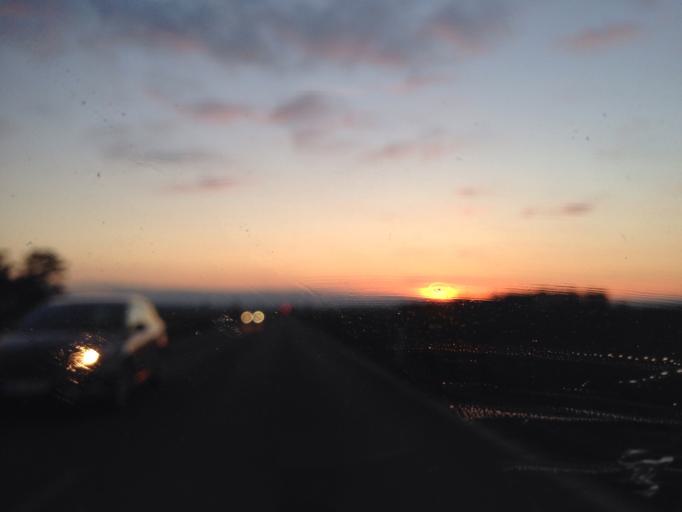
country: CZ
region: Central Bohemia
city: Rakovnik
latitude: 50.1703
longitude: 13.6740
